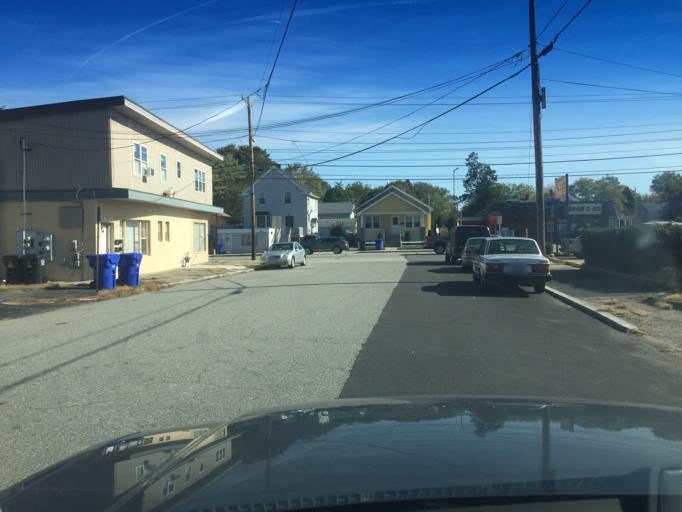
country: US
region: Rhode Island
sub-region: Providence County
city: East Providence
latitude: 41.8322
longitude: -71.3617
